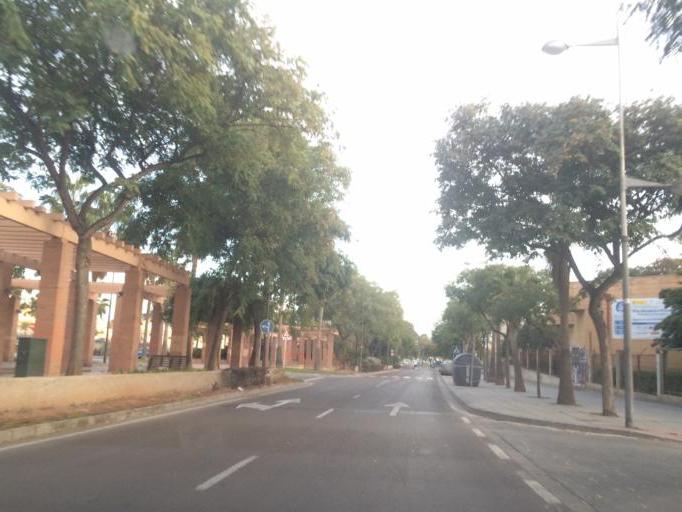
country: ES
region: Andalusia
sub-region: Provincia de Almeria
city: Almeria
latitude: 36.8502
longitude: -2.4646
